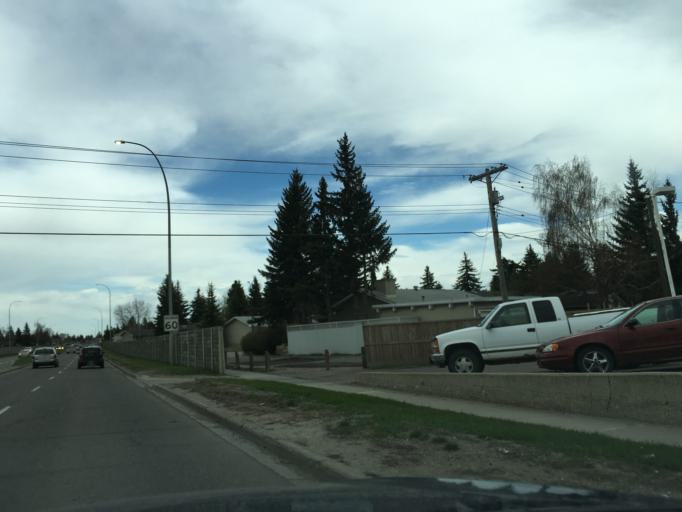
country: CA
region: Alberta
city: Calgary
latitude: 50.9640
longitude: -114.0582
